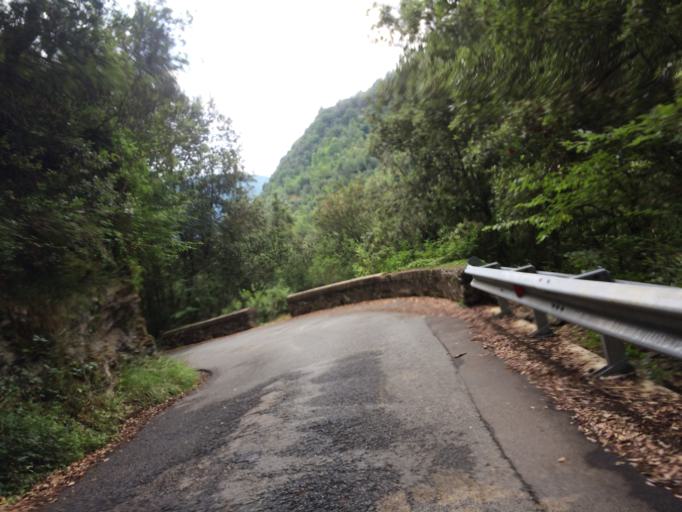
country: IT
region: Liguria
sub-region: Provincia di Imperia
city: Castel Vittorio
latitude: 43.9418
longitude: 7.6857
